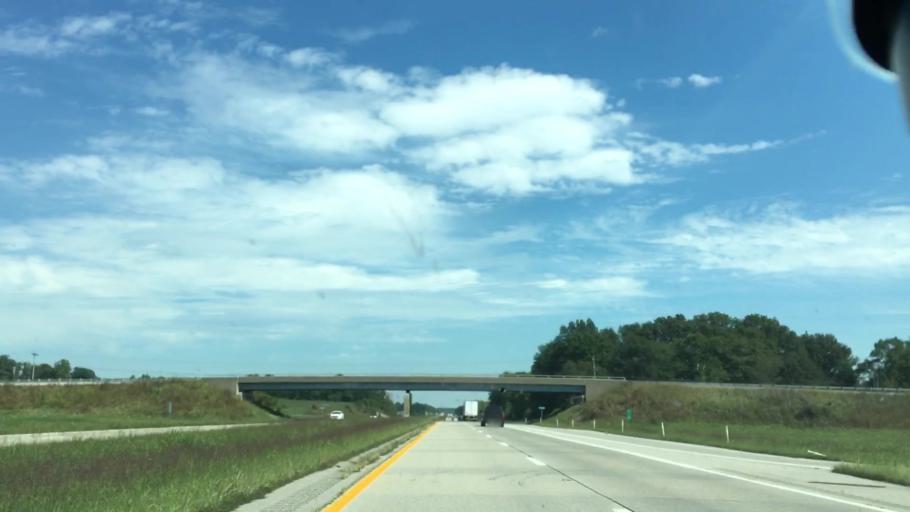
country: US
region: Kentucky
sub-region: Daviess County
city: Owensboro
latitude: 37.7562
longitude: -87.2618
